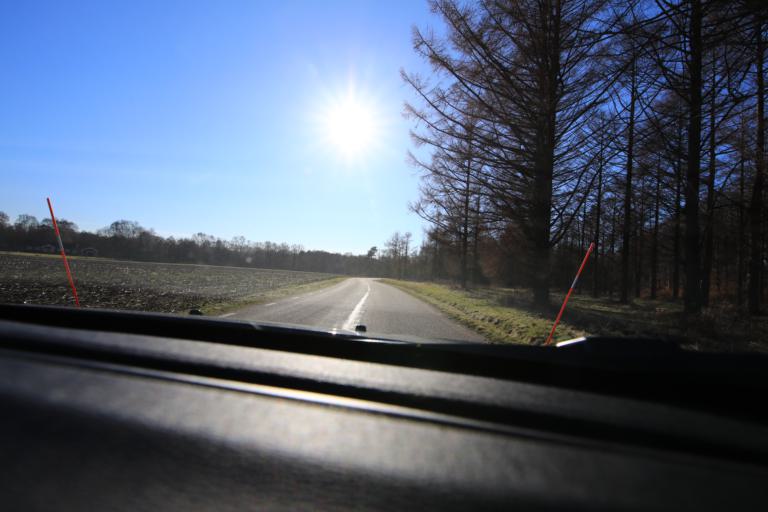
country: SE
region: Halland
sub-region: Varbergs Kommun
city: Tvaaker
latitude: 57.0629
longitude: 12.4600
